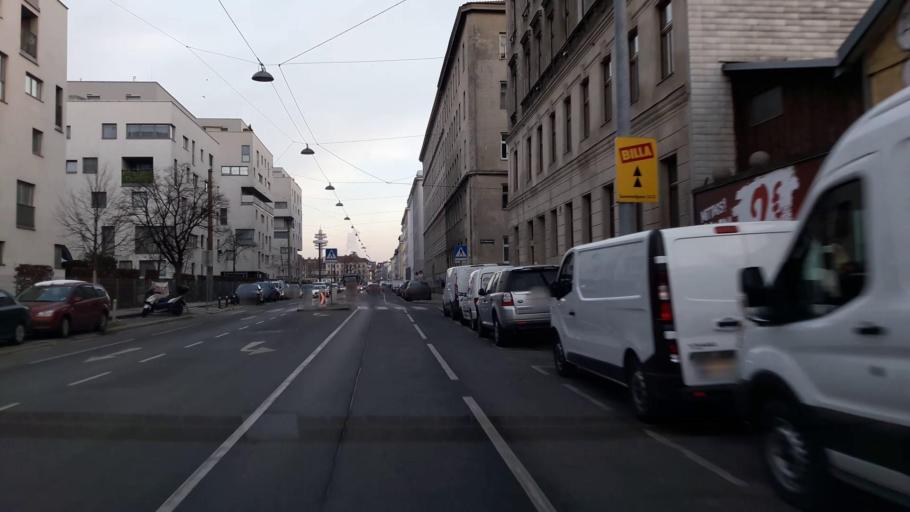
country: AT
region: Vienna
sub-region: Wien Stadt
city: Vienna
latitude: 48.1815
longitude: 16.3679
